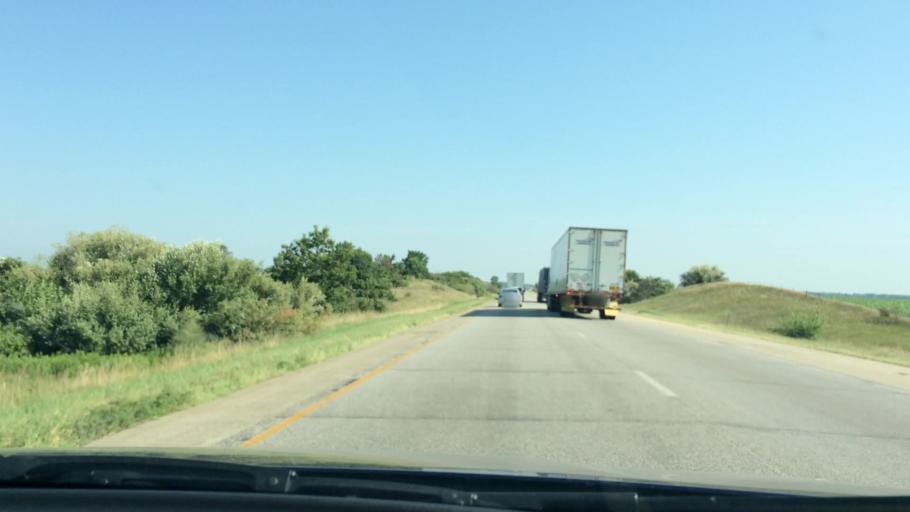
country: US
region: Indiana
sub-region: Newton County
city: Roselawn
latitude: 41.0448
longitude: -87.2703
